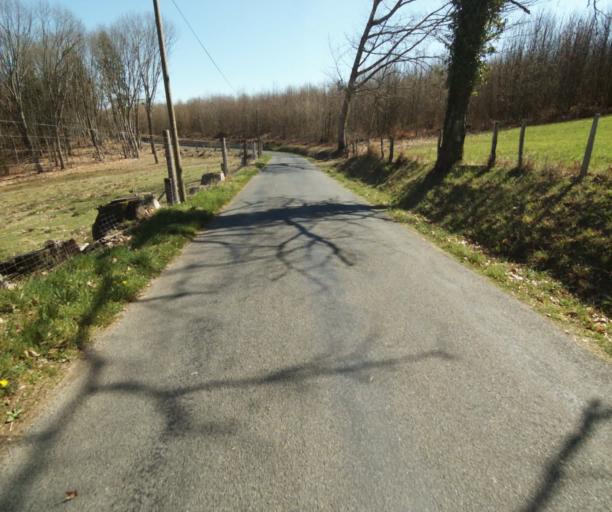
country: FR
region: Limousin
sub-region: Departement de la Correze
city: Chameyrat
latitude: 45.2717
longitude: 1.7046
